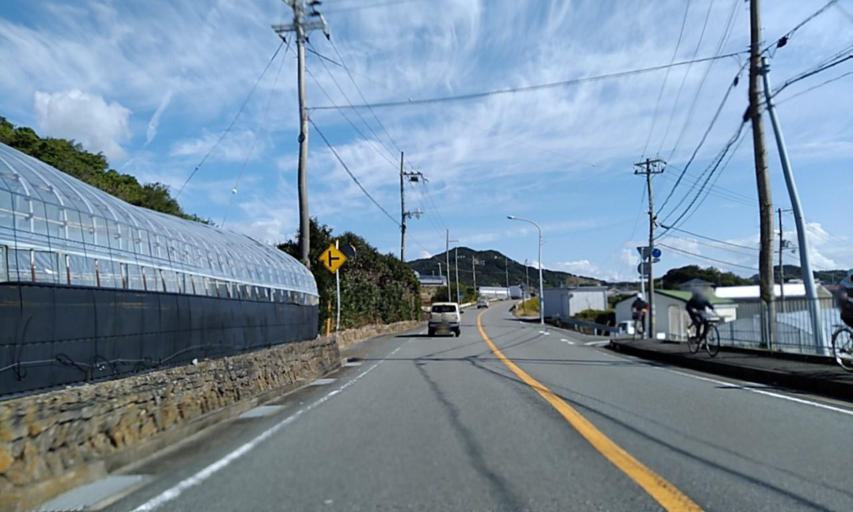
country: JP
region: Wakayama
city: Gobo
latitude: 33.8453
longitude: 135.1697
